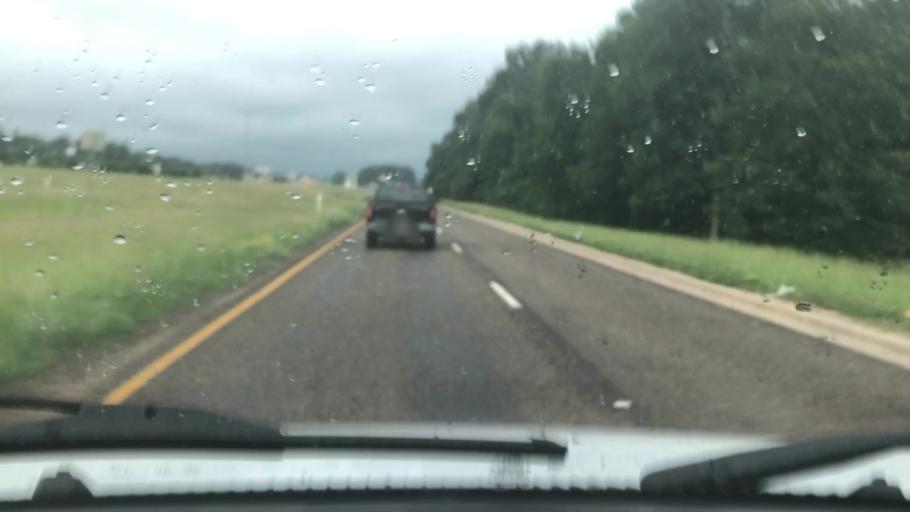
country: US
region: Texas
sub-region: Bowie County
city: Wake Village
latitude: 33.4385
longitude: -94.0974
